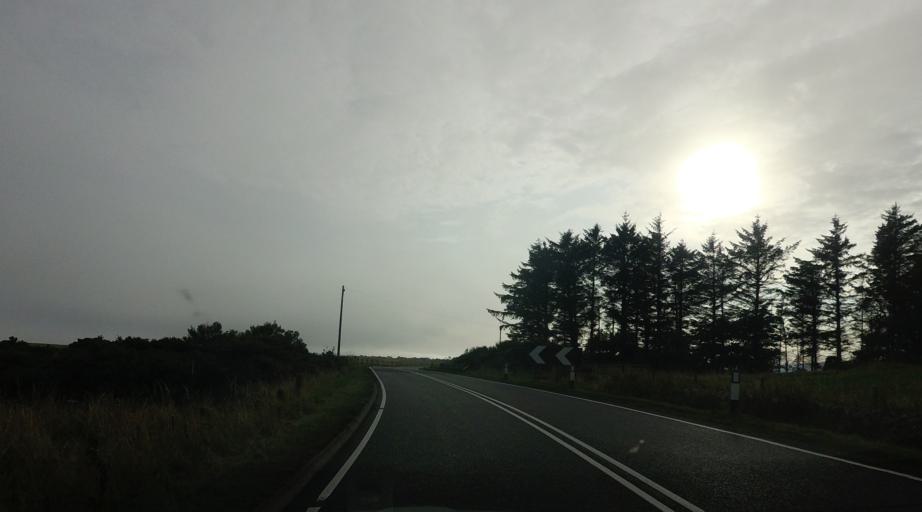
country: GB
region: Scotland
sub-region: Highland
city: Brora
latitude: 58.0364
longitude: -3.8379
